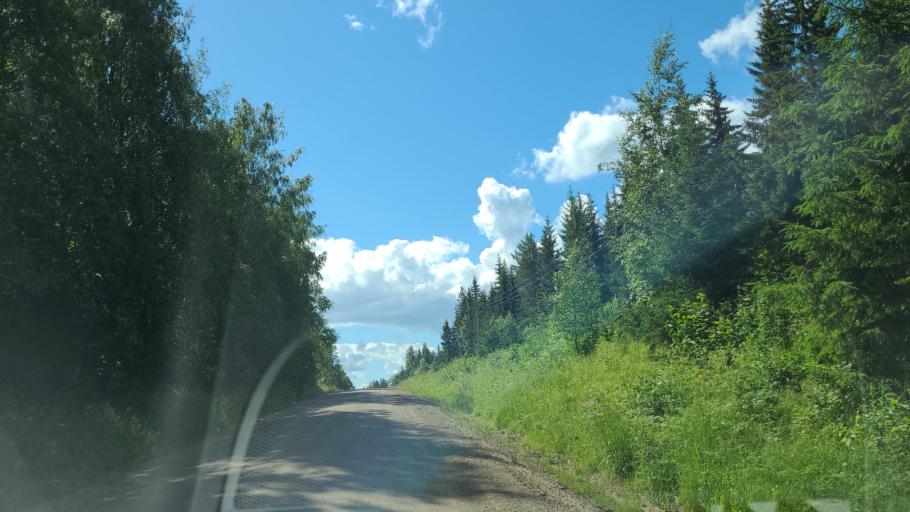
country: FI
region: Northern Savo
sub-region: Koillis-Savo
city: Kaavi
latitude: 62.9466
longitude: 28.7648
